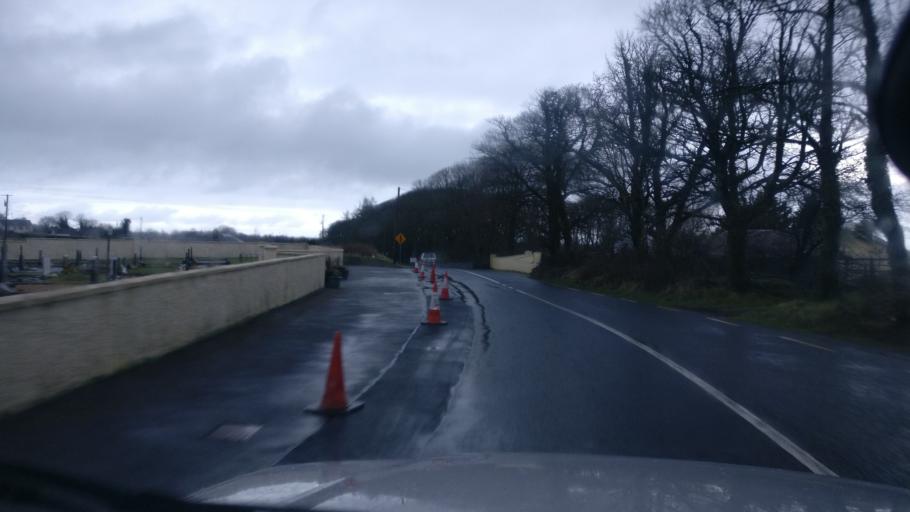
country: IE
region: Connaught
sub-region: County Galway
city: Ballinasloe
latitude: 53.3247
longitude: -8.4065
